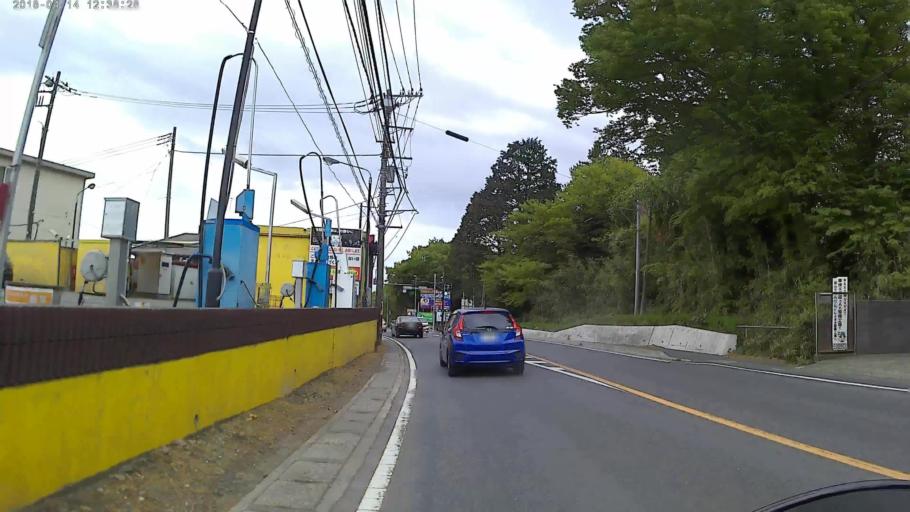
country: JP
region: Kanagawa
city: Atsugi
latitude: 35.4094
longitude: 139.4063
